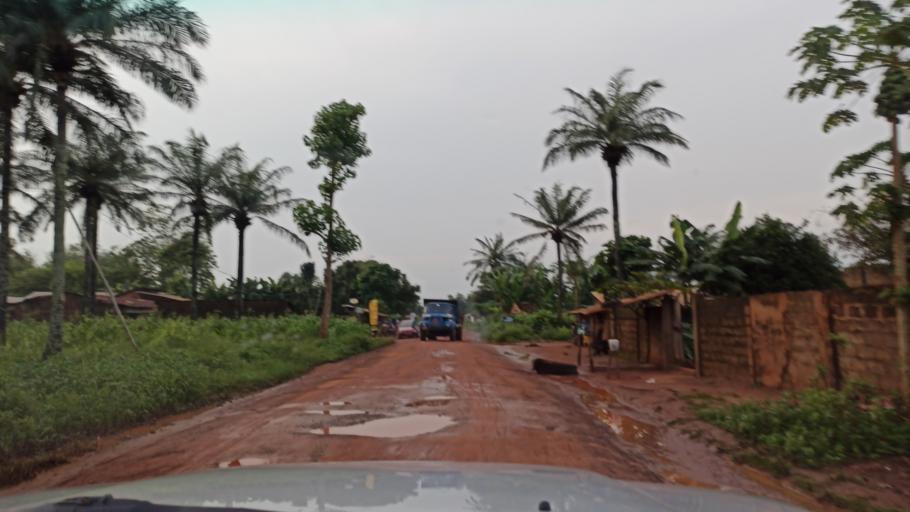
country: BJ
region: Queme
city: Porto-Novo
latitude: 6.5448
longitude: 2.6177
